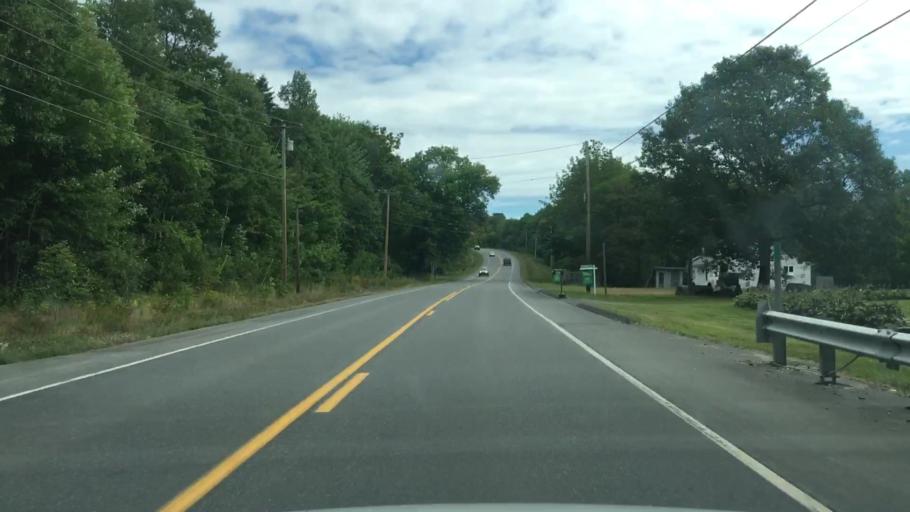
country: US
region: Maine
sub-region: Piscataquis County
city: Milo
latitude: 45.2422
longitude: -69.0250
